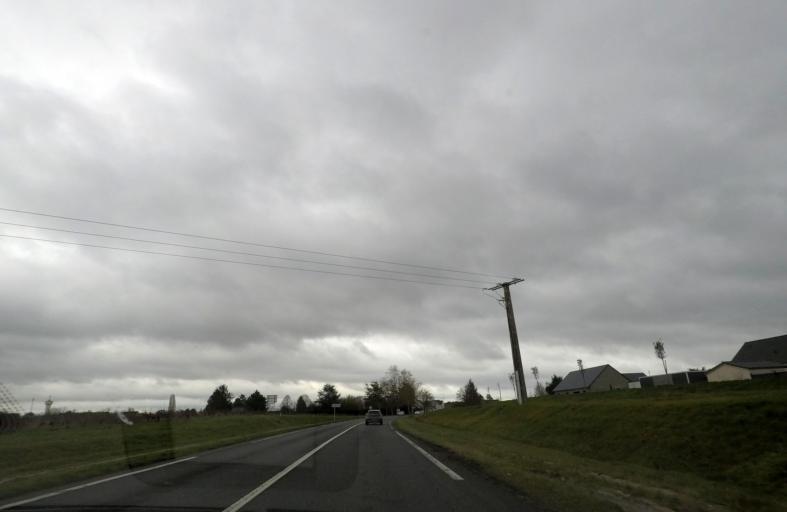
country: FR
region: Centre
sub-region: Departement du Loir-et-Cher
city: Cour-Cheverny
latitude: 47.5163
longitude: 1.4520
